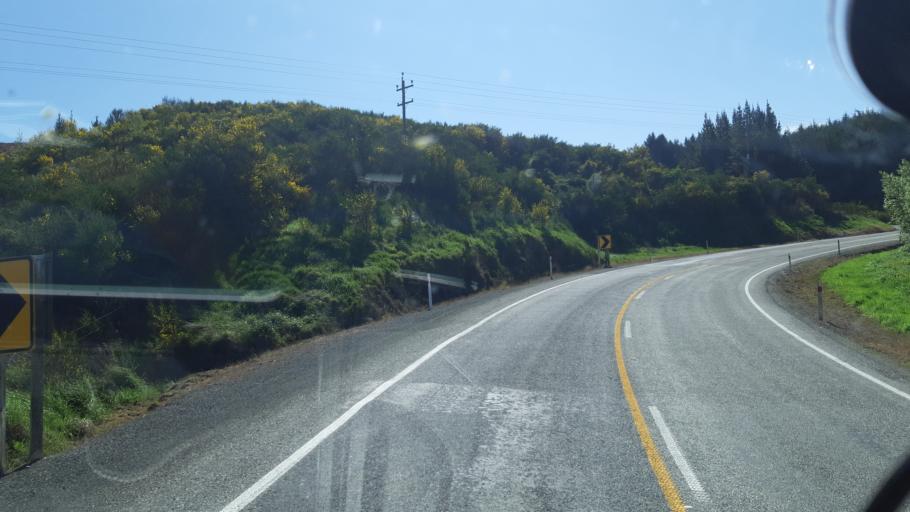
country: NZ
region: Otago
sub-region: Clutha District
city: Milton
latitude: -46.0621
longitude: 169.8130
